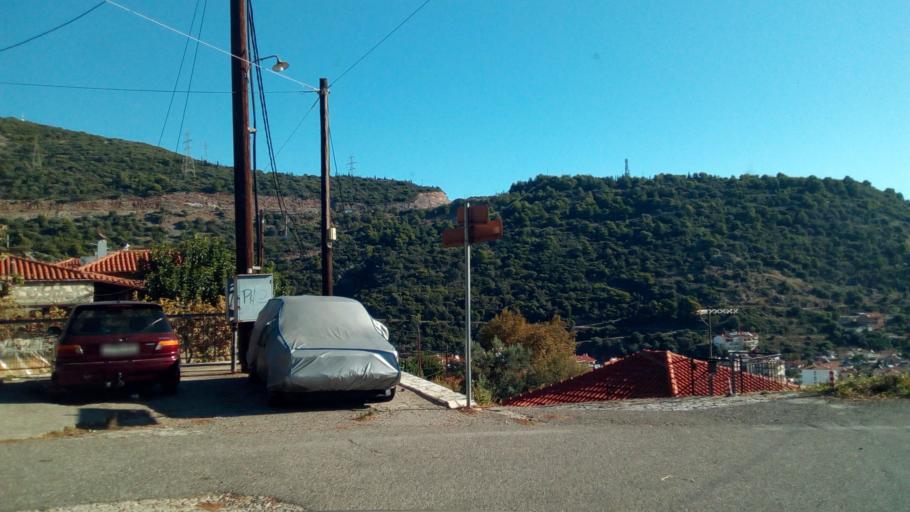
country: GR
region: West Greece
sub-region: Nomos Aitolias kai Akarnanias
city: Nafpaktos
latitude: 38.3949
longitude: 21.8273
